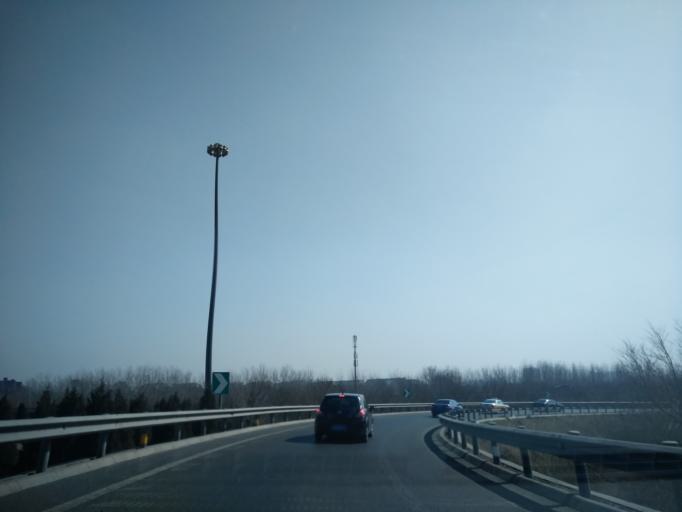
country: CN
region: Beijing
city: Jiugong
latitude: 39.8189
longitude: 116.5010
